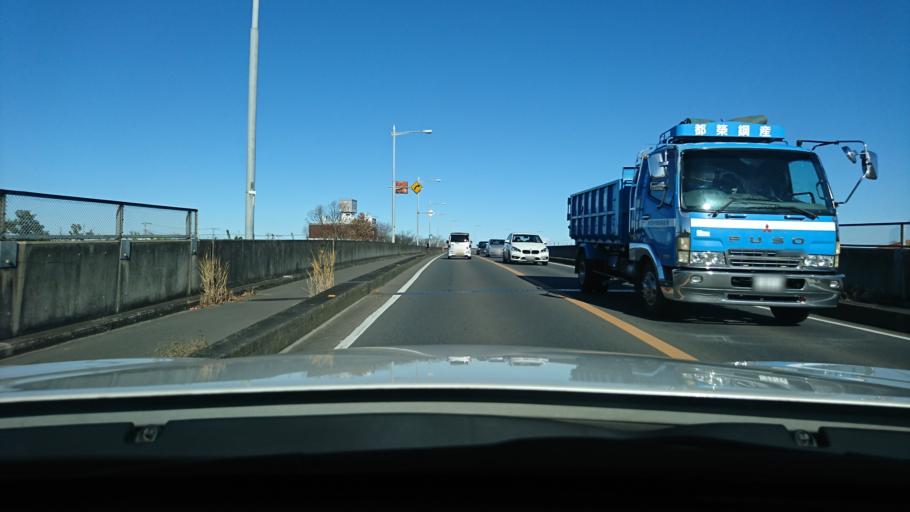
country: JP
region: Saitama
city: Kamifukuoka
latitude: 35.8882
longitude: 139.5583
